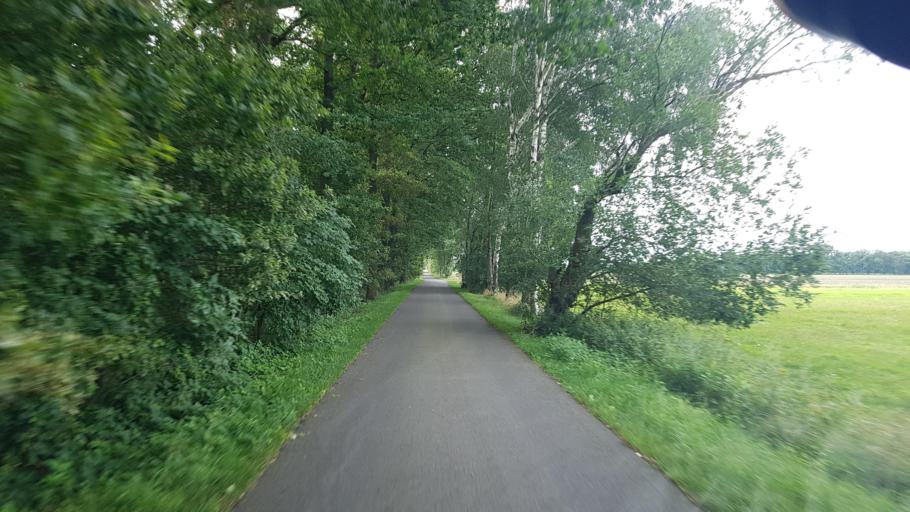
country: DE
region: Brandenburg
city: Bronkow
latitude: 51.6145
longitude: 13.9459
